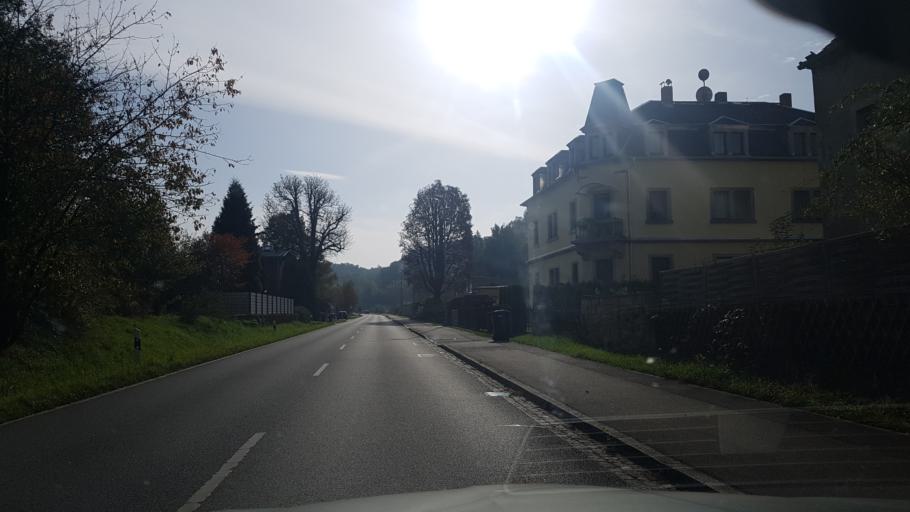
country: DE
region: Saxony
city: Dohma
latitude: 50.9204
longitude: 13.9644
